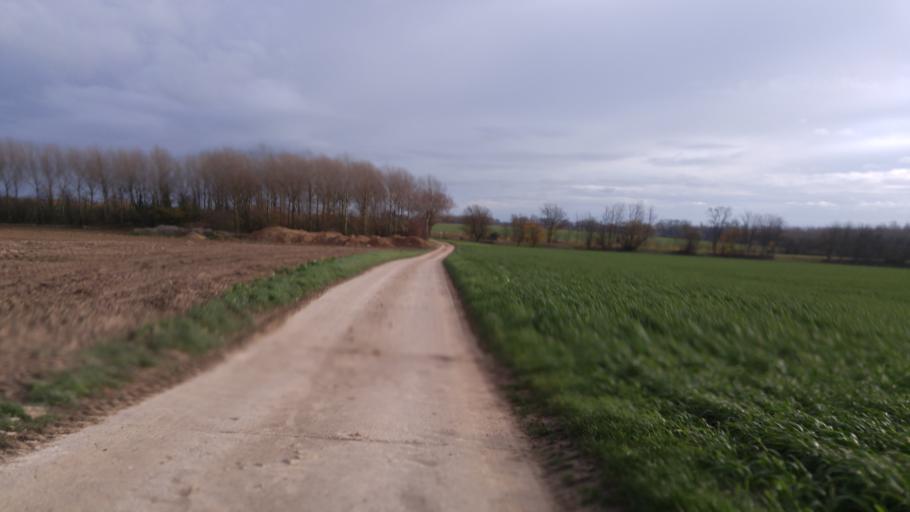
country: BE
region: Wallonia
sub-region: Province du Brabant Wallon
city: Ramillies
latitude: 50.6225
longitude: 4.8983
